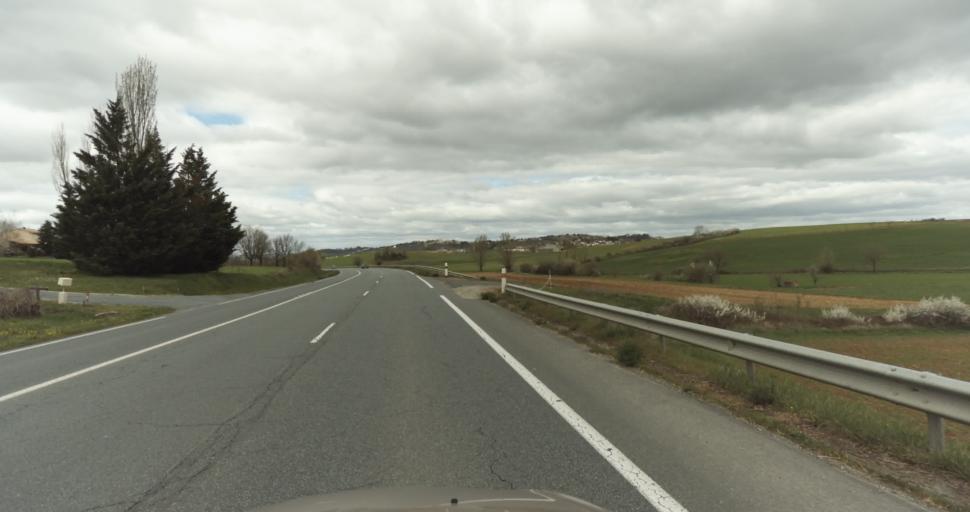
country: FR
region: Midi-Pyrenees
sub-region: Departement du Tarn
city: Puygouzon
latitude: 43.8765
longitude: 2.1775
